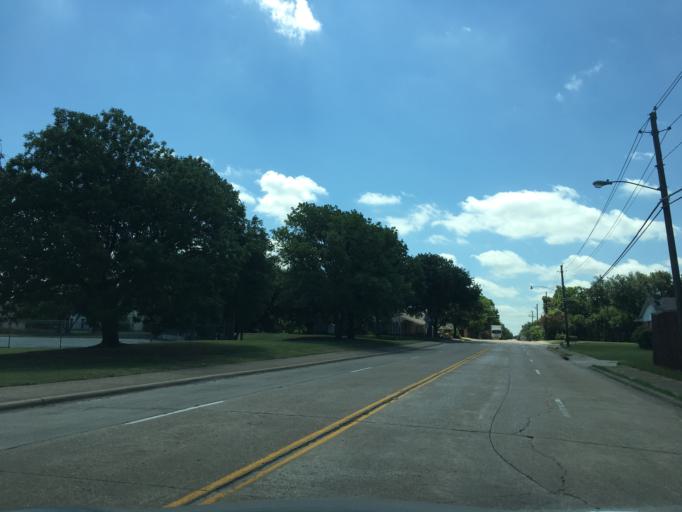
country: US
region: Texas
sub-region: Dallas County
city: Garland
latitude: 32.8440
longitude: -96.6556
